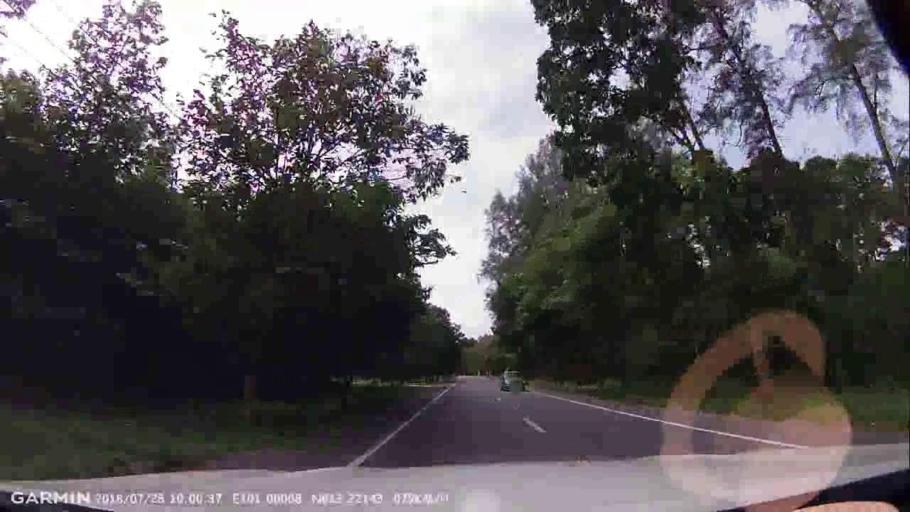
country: TH
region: Chon Buri
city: Si Racha
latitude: 13.2210
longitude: 101.0001
